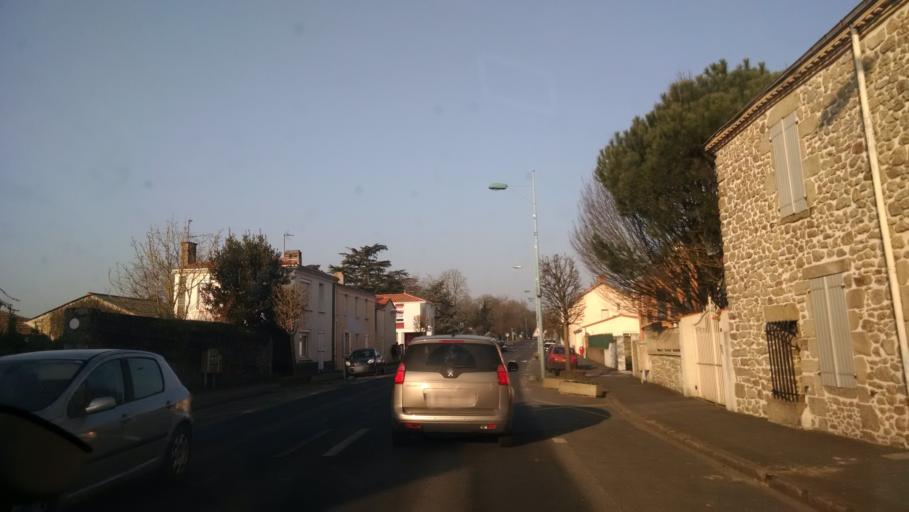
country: FR
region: Pays de la Loire
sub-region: Departement de la Loire-Atlantique
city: Aigrefeuille-sur-Maine
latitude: 47.0771
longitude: -1.4019
